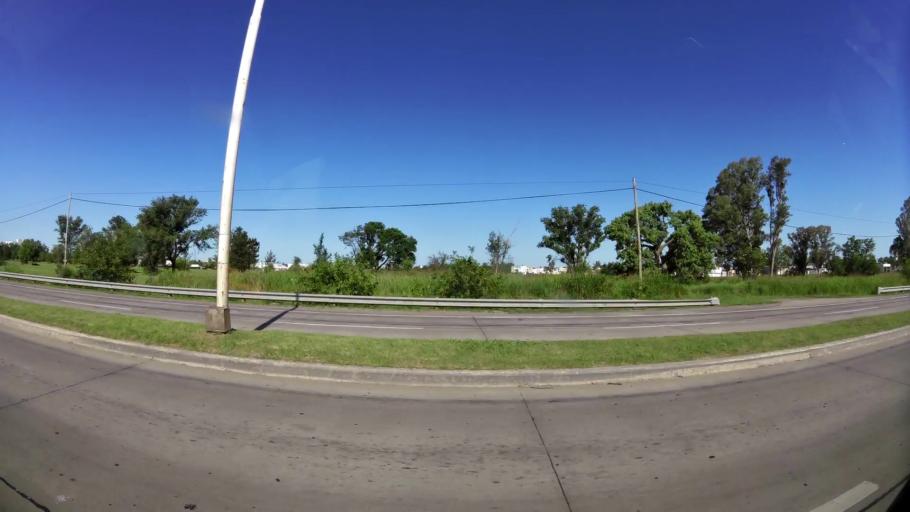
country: AR
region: Santa Fe
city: Rafaela
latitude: -31.2643
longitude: -61.5081
